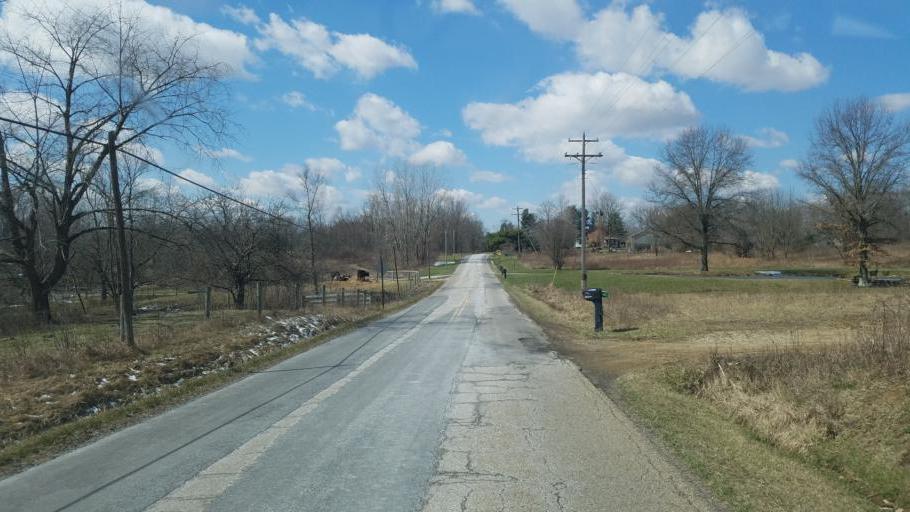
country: US
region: Ohio
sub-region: Knox County
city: Mount Vernon
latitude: 40.3142
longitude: -82.5360
